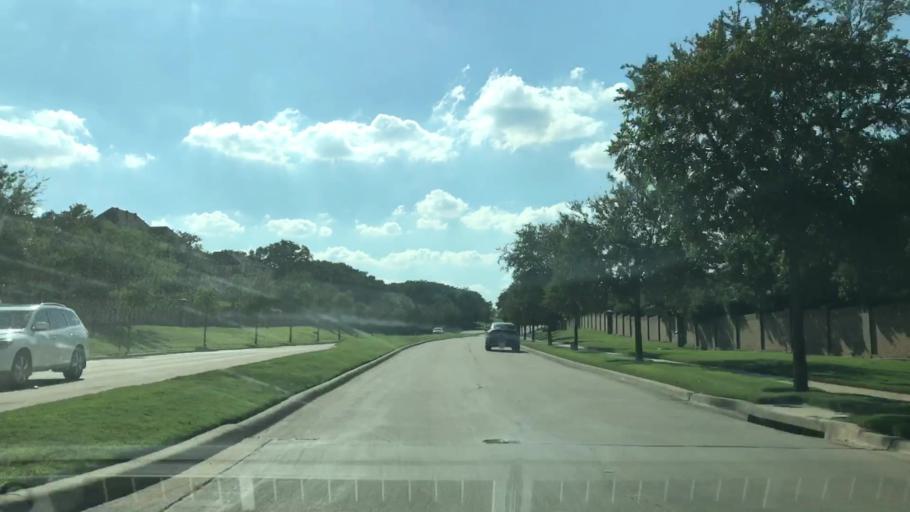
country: US
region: Texas
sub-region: Tarrant County
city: Keller
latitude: 32.9204
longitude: -97.1993
